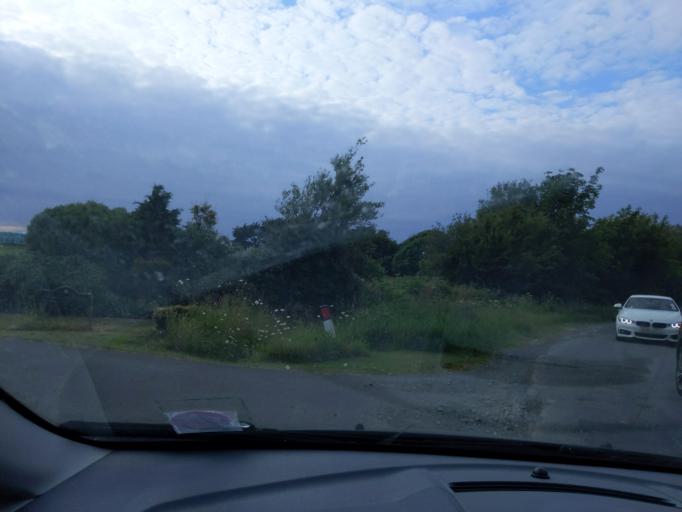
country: IM
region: Ramsey
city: Ramsey
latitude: 54.3898
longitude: -4.4477
